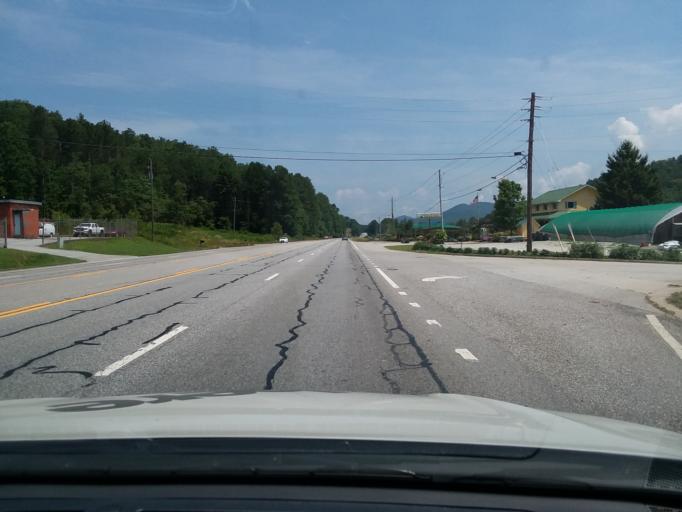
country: US
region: Georgia
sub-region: Rabun County
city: Mountain City
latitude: 34.9433
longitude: -83.3876
